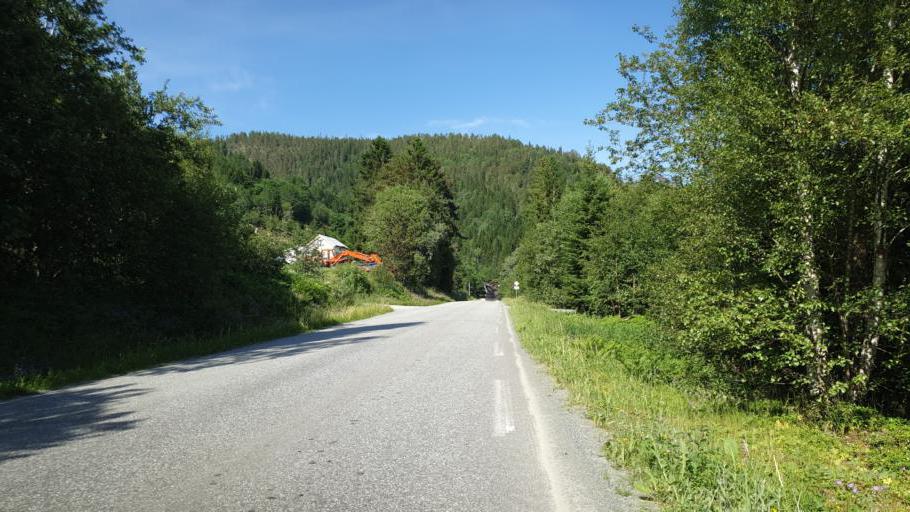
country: NO
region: Nord-Trondelag
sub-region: Leksvik
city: Leksvik
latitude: 63.6328
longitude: 10.5715
